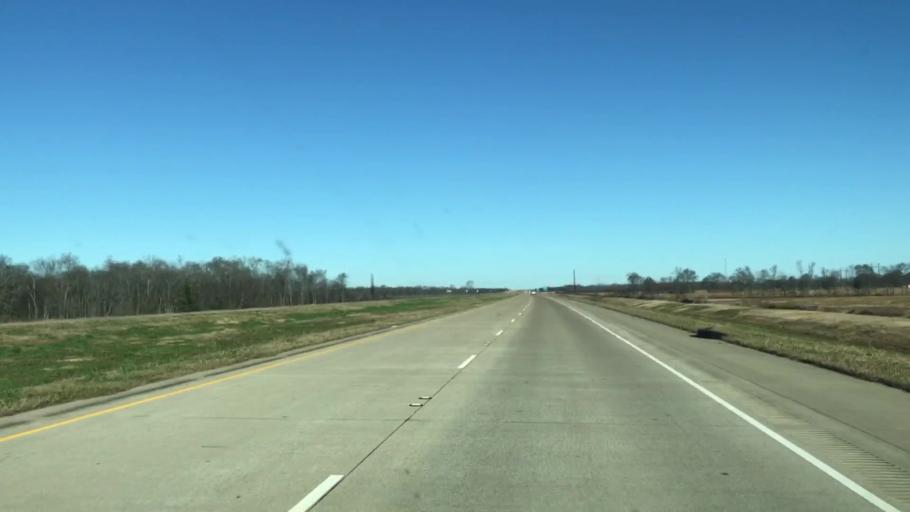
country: US
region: Louisiana
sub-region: Caddo Parish
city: Blanchard
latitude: 32.6574
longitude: -93.8429
